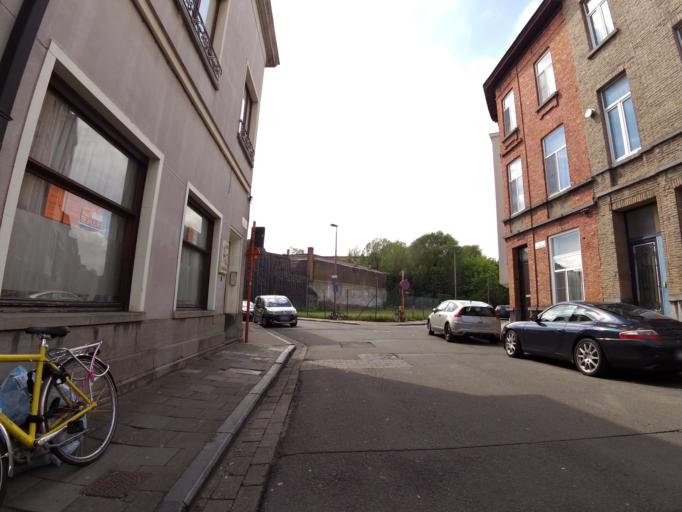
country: BE
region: Flanders
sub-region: Provincie Oost-Vlaanderen
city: Gent
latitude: 51.0550
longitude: 3.7124
